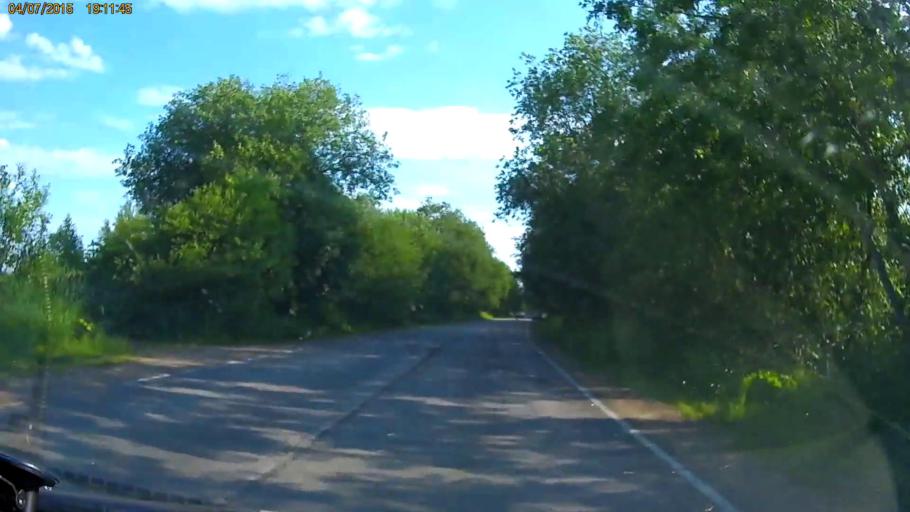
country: RU
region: Leningrad
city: Garbolovo
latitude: 60.3237
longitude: 30.4943
